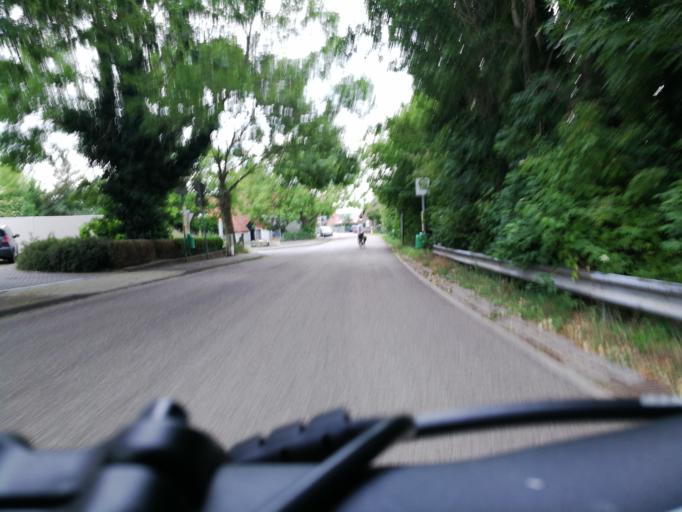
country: DE
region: North Rhine-Westphalia
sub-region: Regierungsbezirk Dusseldorf
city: Kleve
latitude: 51.8264
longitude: 6.1415
